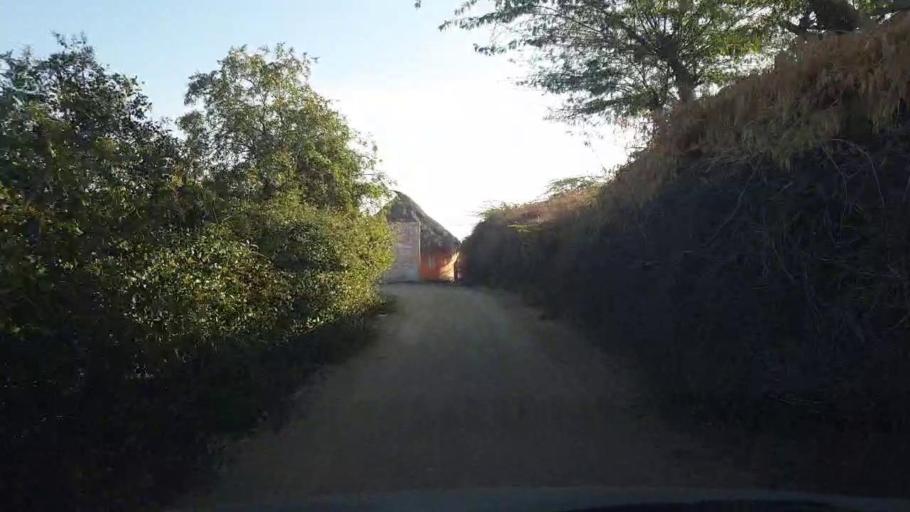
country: PK
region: Sindh
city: Dhoro Naro
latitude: 25.4332
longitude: 69.5321
